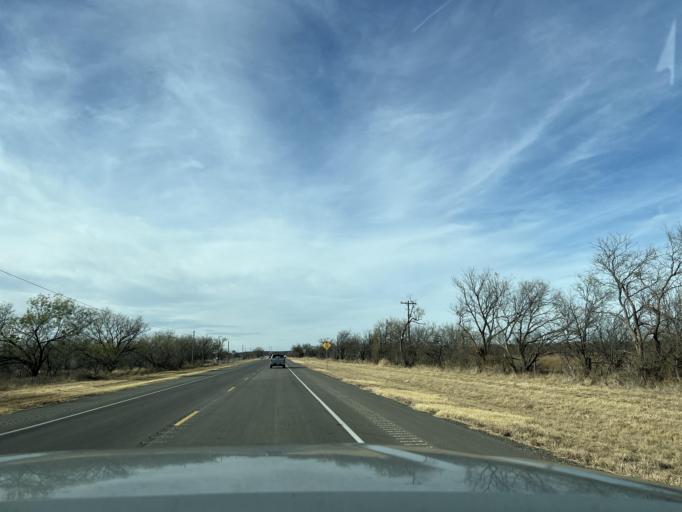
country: US
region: Texas
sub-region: Shackelford County
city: Albany
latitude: 32.7147
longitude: -99.2824
